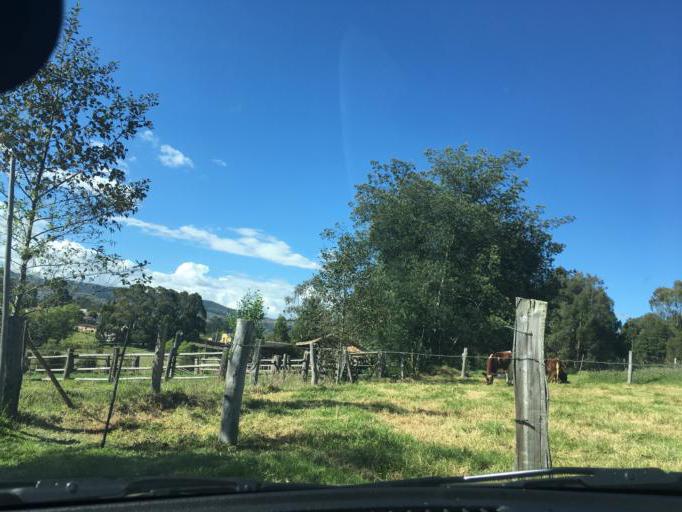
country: CO
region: Boyaca
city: Firavitoba
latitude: 5.6709
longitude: -72.9558
